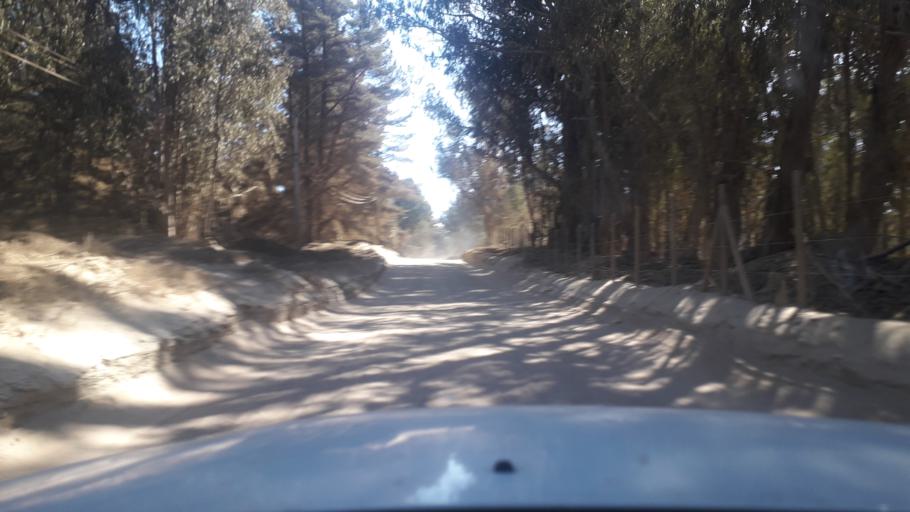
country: CL
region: Valparaiso
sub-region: Provincia de Valparaiso
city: Vina del Mar
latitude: -32.9569
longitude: -71.5189
